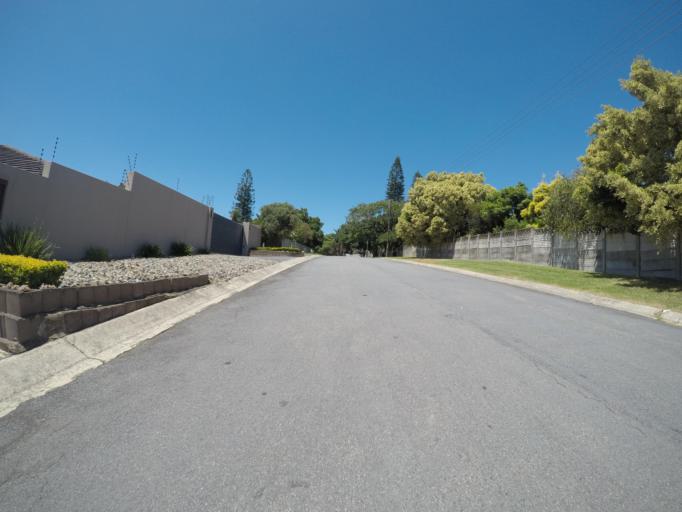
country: ZA
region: Eastern Cape
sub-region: Buffalo City Metropolitan Municipality
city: East London
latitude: -32.9651
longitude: 27.9459
